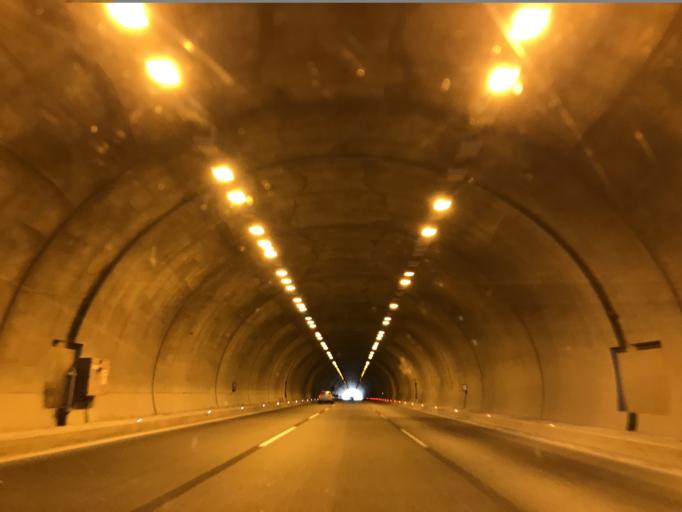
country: TR
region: Bursa
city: Gursu
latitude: 40.2542
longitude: 29.2175
